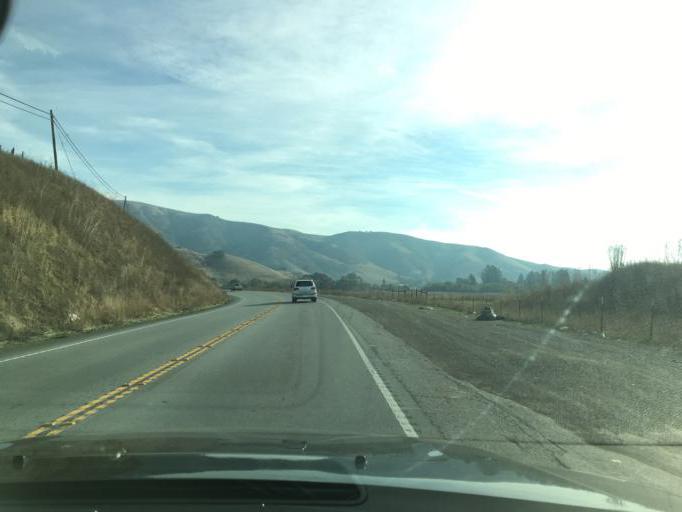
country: US
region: California
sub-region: Santa Clara County
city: Gilroy
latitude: 36.9877
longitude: -121.4562
